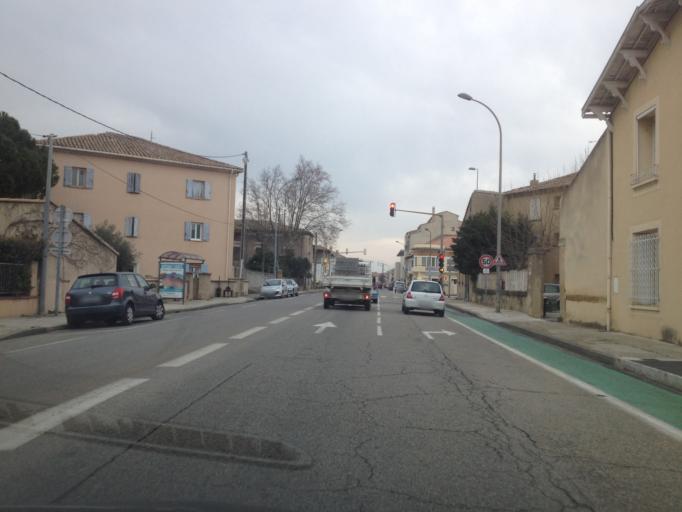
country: FR
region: Provence-Alpes-Cote d'Azur
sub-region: Departement du Vaucluse
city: Sorgues
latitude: 44.0042
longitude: 4.8700
